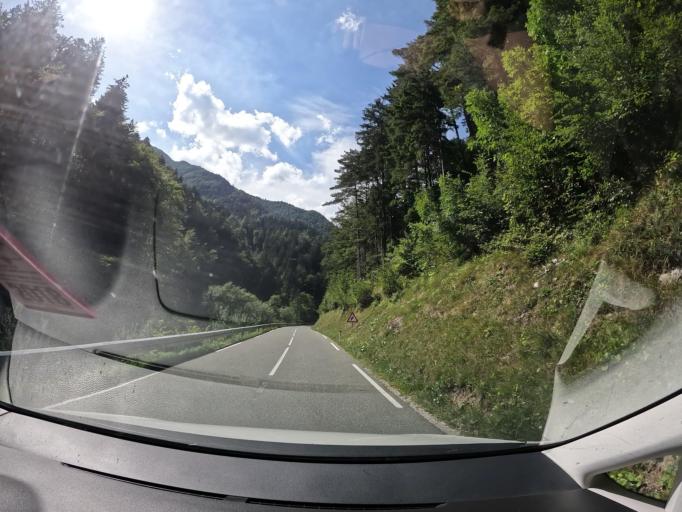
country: SI
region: Jezersko
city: Zgornje Jezersko
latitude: 46.3645
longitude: 14.4512
